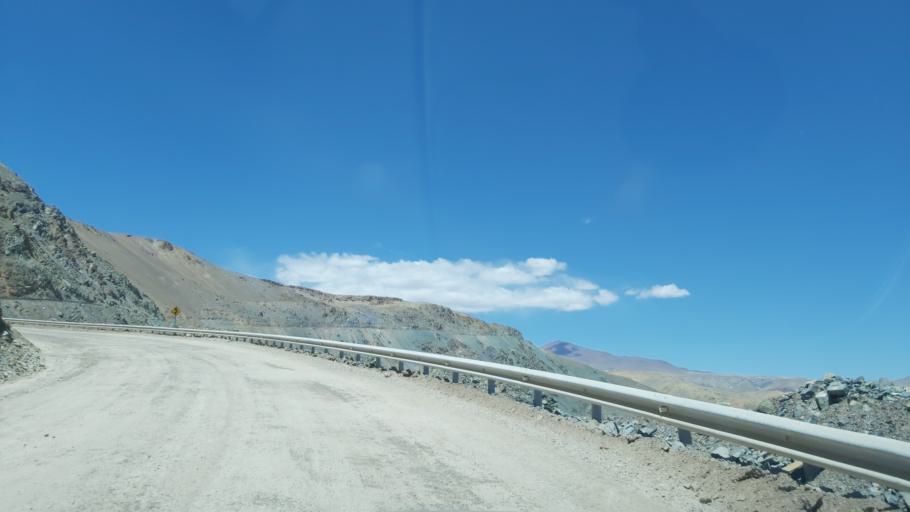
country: CL
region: Atacama
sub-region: Provincia de Chanaral
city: Diego de Almagro
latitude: -26.4568
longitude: -69.3133
